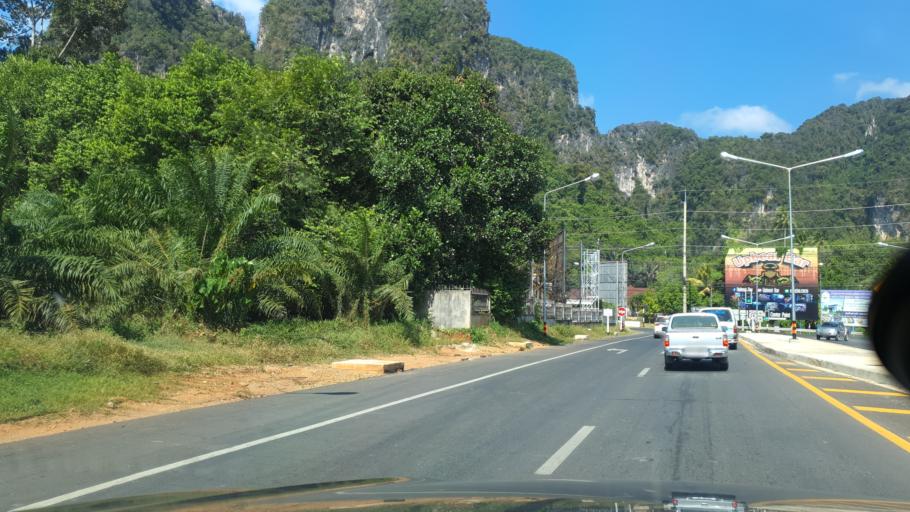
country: TH
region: Krabi
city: Krabi
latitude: 8.0790
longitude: 98.8561
